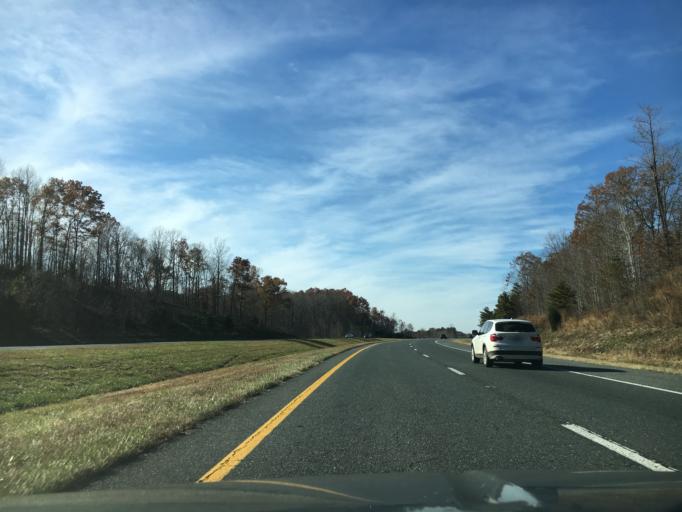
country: US
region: Virginia
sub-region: Amherst County
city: Madison Heights
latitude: 37.3854
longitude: -79.0847
